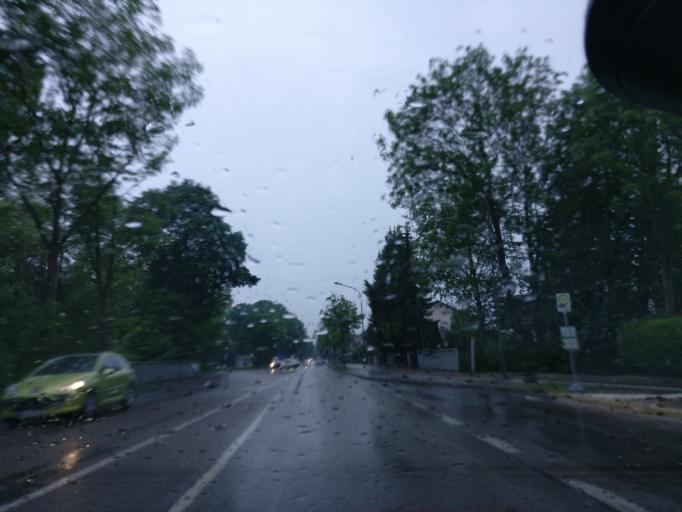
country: DE
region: Bavaria
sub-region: Upper Bavaria
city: Dachau
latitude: 48.2564
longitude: 11.4648
